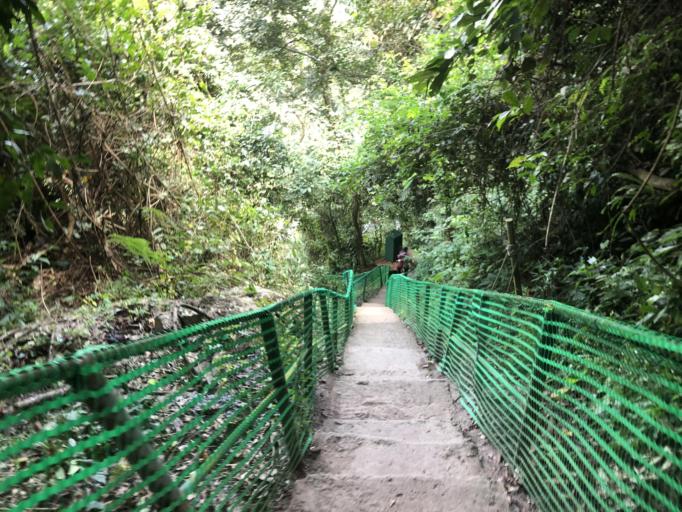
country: TG
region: Plateaux
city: Kpalime
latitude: 6.8444
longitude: 0.4472
